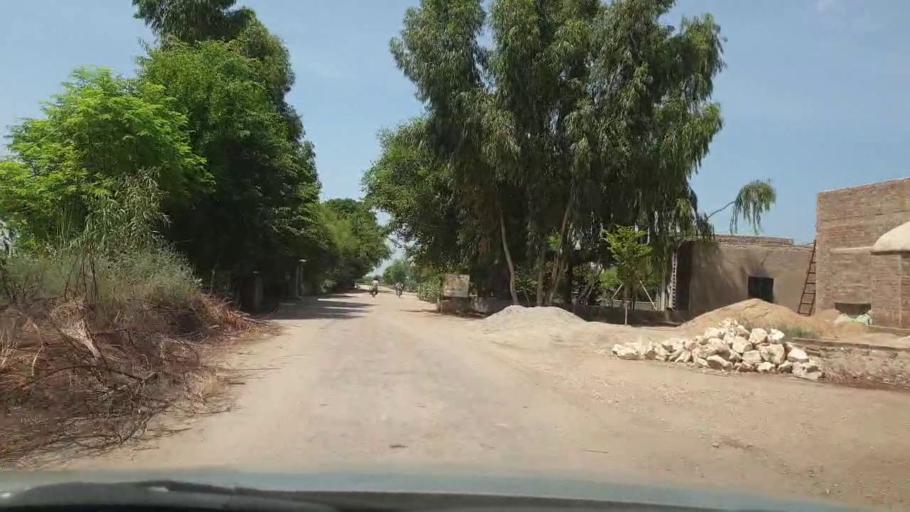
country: PK
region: Sindh
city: Pano Aqil
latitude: 27.6909
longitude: 69.1107
